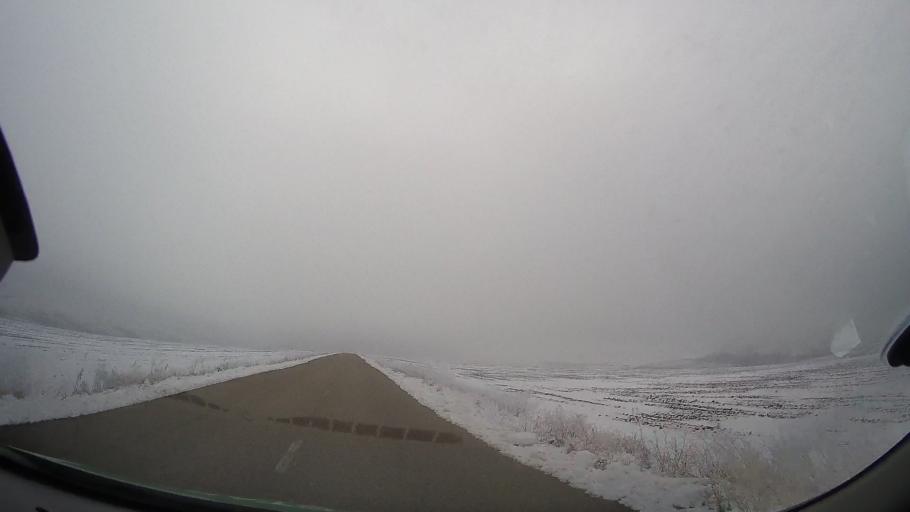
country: RO
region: Vaslui
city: Coroiesti
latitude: 46.2229
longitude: 27.4787
